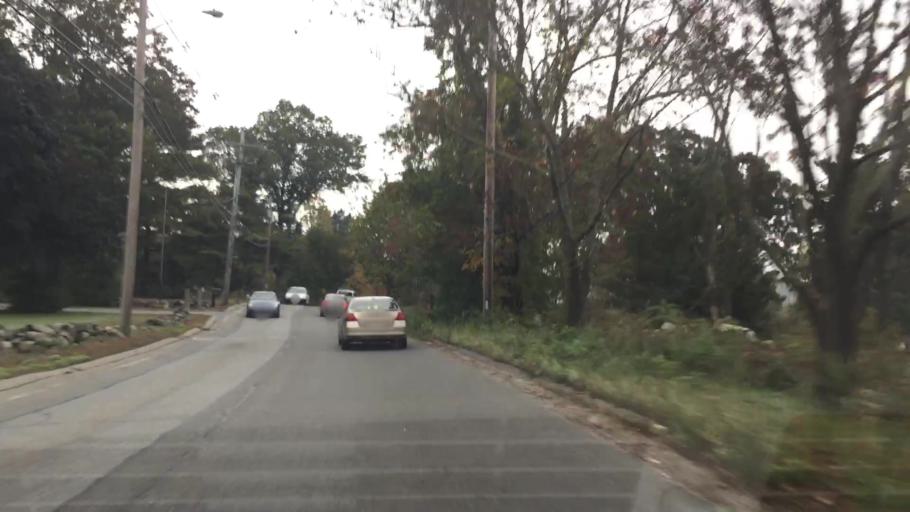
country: US
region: Massachusetts
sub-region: Middlesex County
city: Dracut
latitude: 42.6998
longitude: -71.2601
